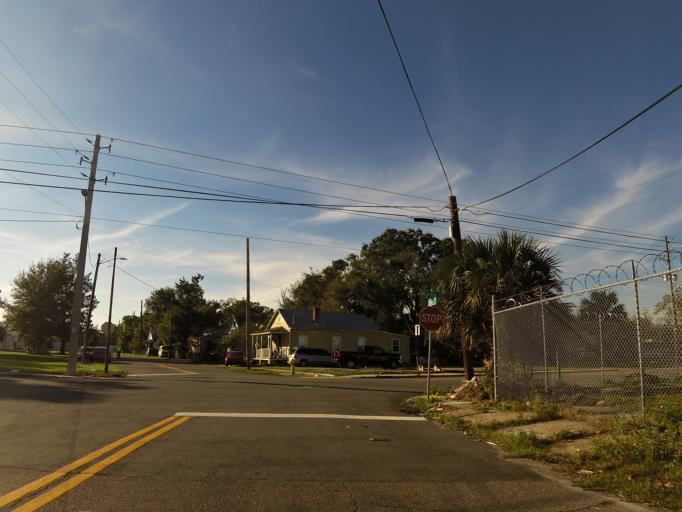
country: US
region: Florida
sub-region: Duval County
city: Jacksonville
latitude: 30.3393
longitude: -81.6755
